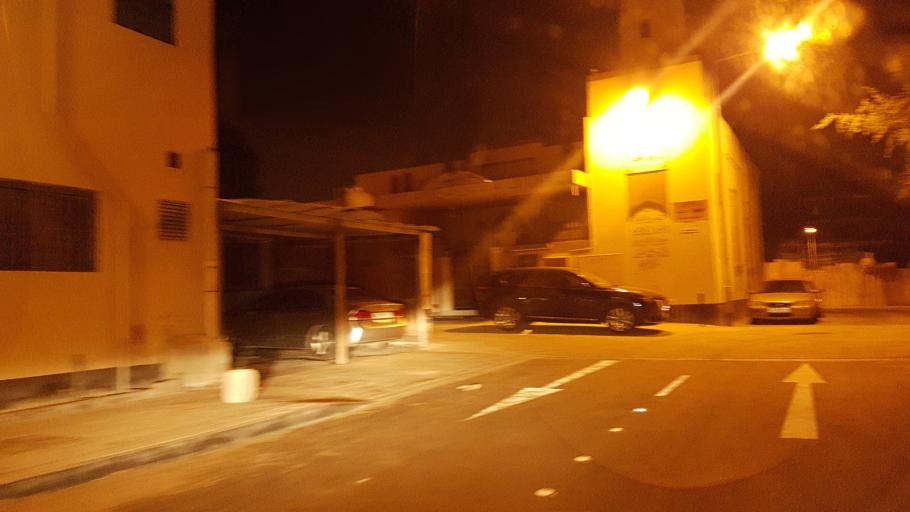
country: BH
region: Manama
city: Jidd Hafs
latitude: 26.2250
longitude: 50.5424
